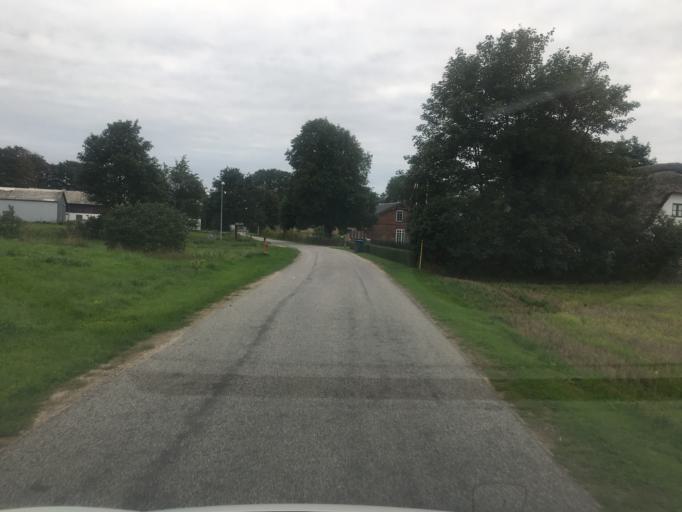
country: DK
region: South Denmark
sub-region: Tonder Kommune
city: Tonder
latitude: 54.9604
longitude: 8.9250
